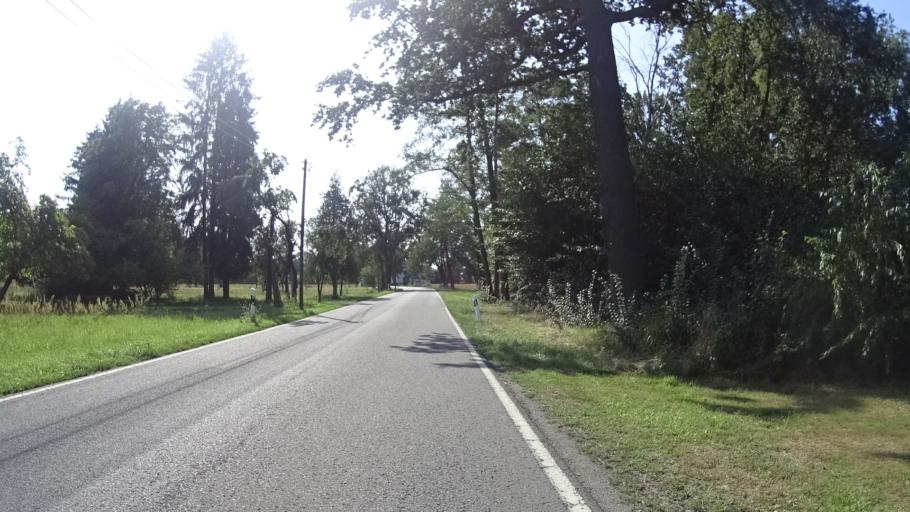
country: DE
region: Brandenburg
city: Burg
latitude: 51.8565
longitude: 14.1308
